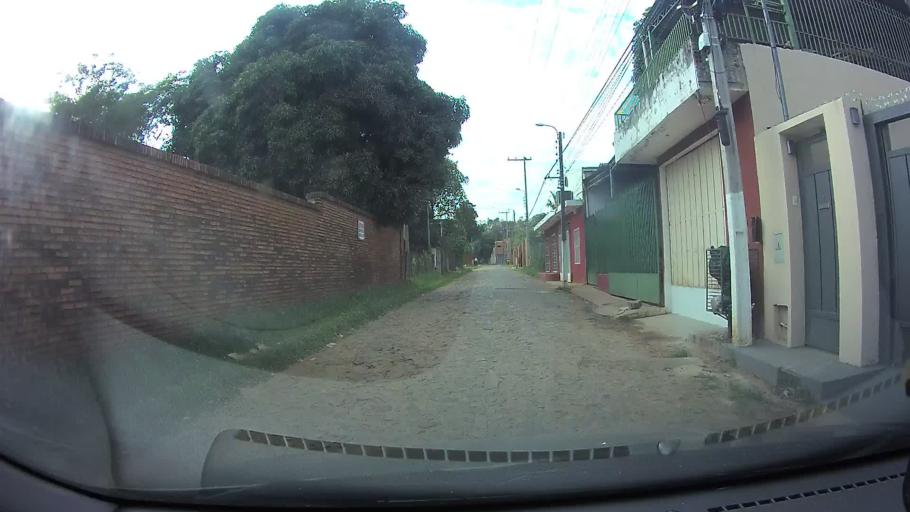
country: PY
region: Central
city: Limpio
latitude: -25.2502
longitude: -57.5091
